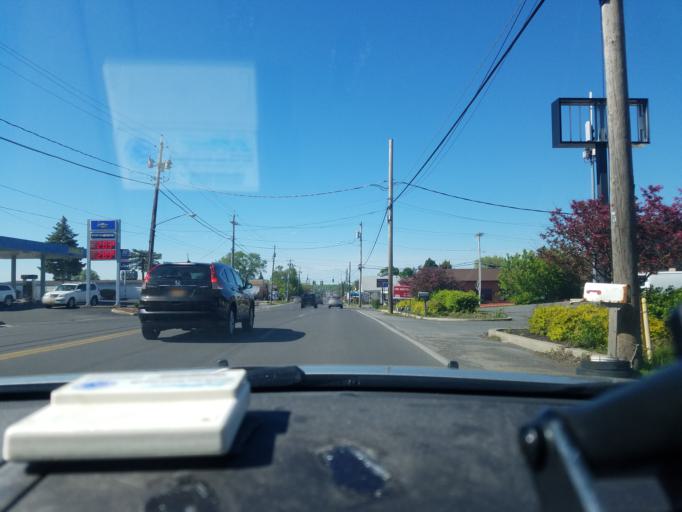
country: US
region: New York
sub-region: Onondaga County
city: Lyncourt
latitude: 43.0734
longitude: -76.1231
